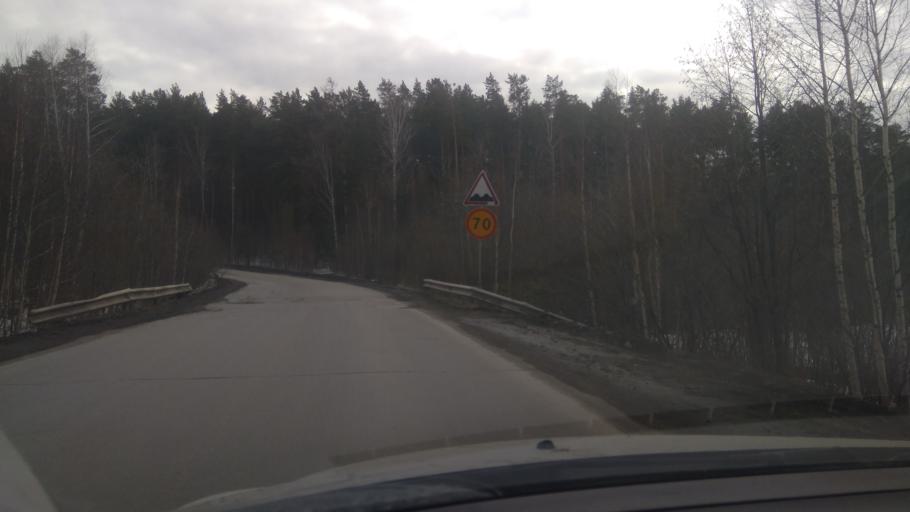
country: RU
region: Sverdlovsk
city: Severka
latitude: 56.8357
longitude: 60.3822
